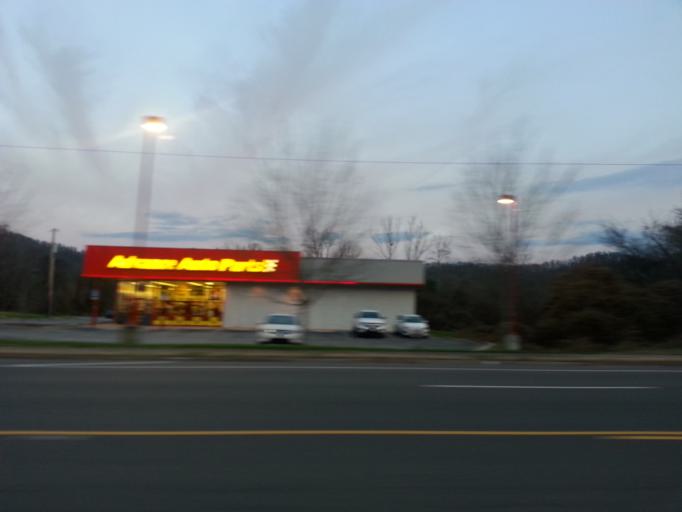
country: US
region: Tennessee
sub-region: McMinn County
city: Etowah
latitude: 35.3401
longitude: -84.5204
